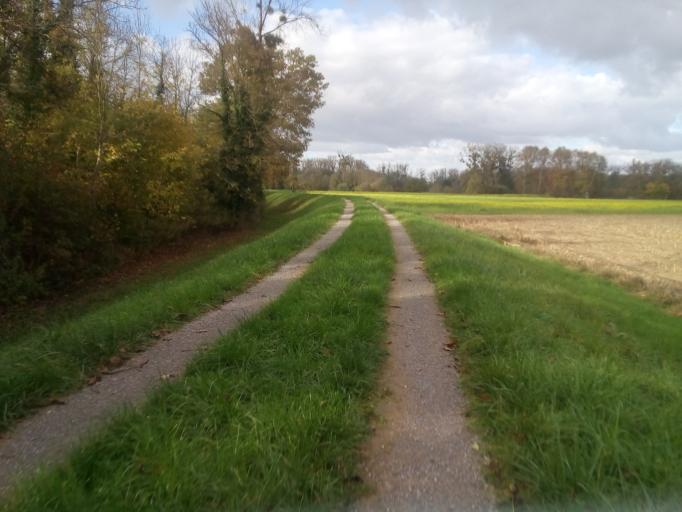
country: DE
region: Baden-Wuerttemberg
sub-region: Karlsruhe Region
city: Lichtenau
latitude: 48.7194
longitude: 7.9758
